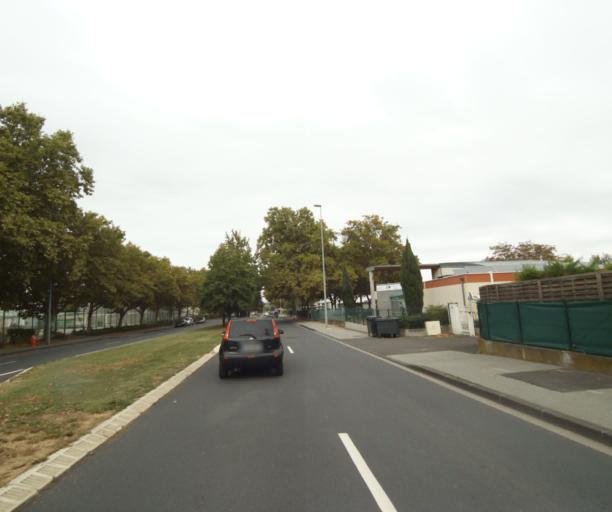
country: FR
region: Auvergne
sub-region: Departement du Puy-de-Dome
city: Gerzat
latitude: 45.7977
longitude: 3.1229
